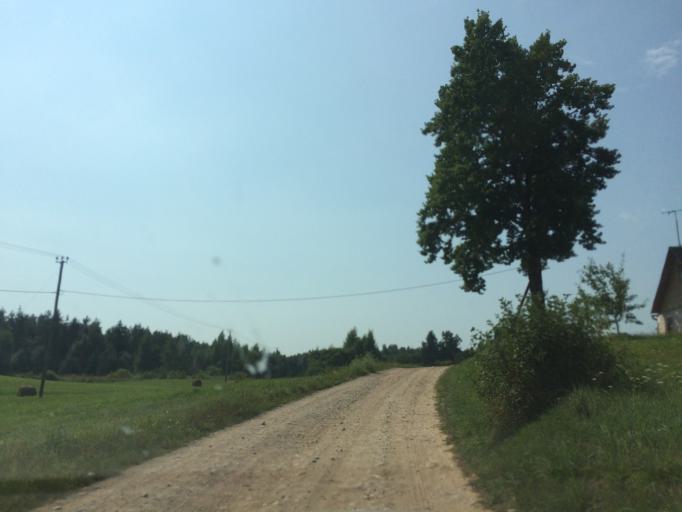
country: LV
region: Ludzas Rajons
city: Ludza
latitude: 56.5406
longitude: 27.5844
